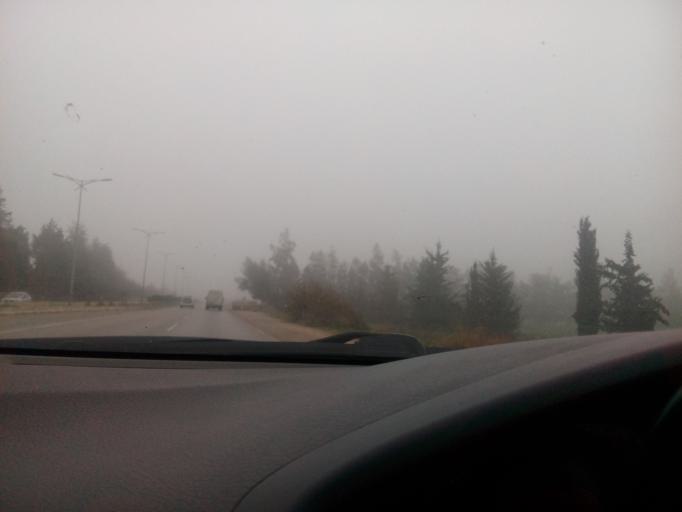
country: DZ
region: Oran
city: Bou Tlelis
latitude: 35.5727
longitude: -0.8668
